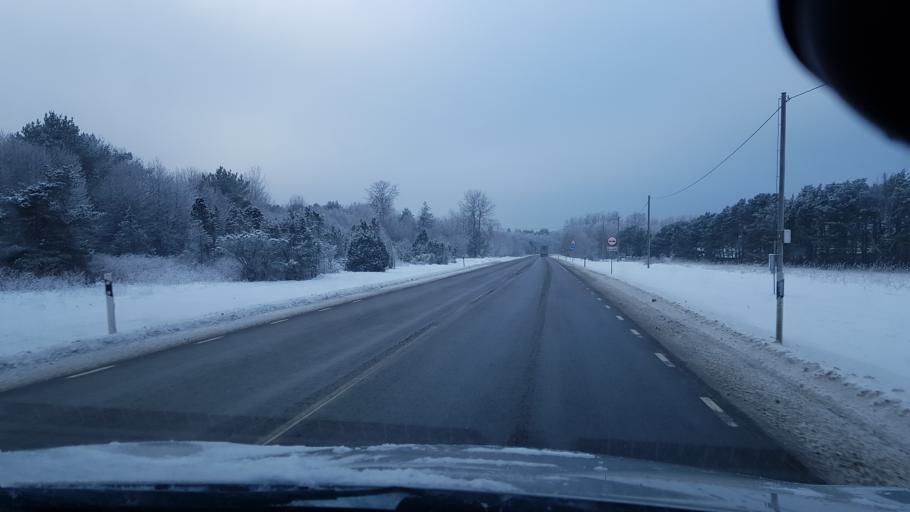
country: EE
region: Harju
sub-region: Paldiski linn
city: Paldiski
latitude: 59.3394
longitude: 24.2110
